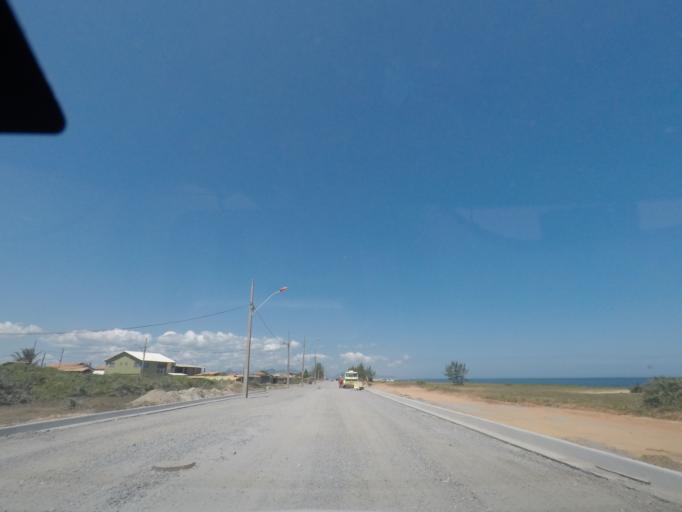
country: BR
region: Rio de Janeiro
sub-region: Marica
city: Marica
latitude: -22.9730
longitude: -42.9096
